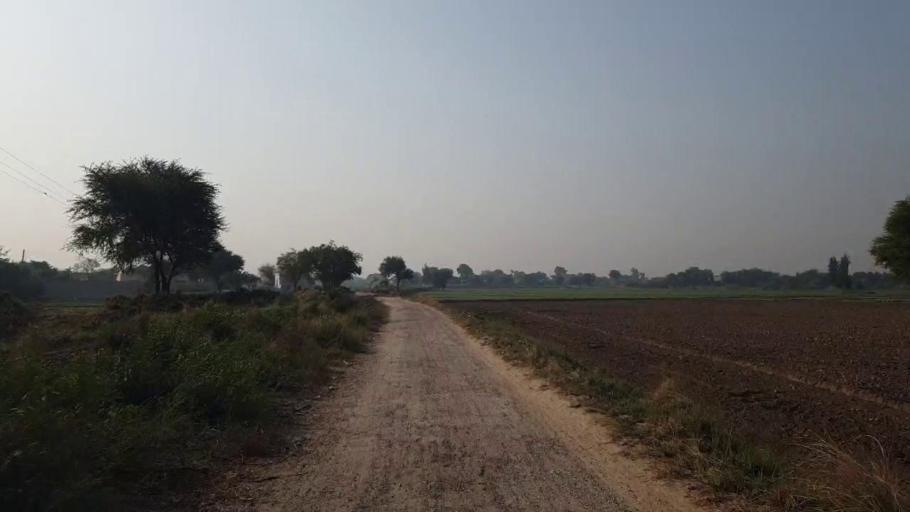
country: PK
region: Sindh
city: Kotri
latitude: 25.3414
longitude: 68.3222
